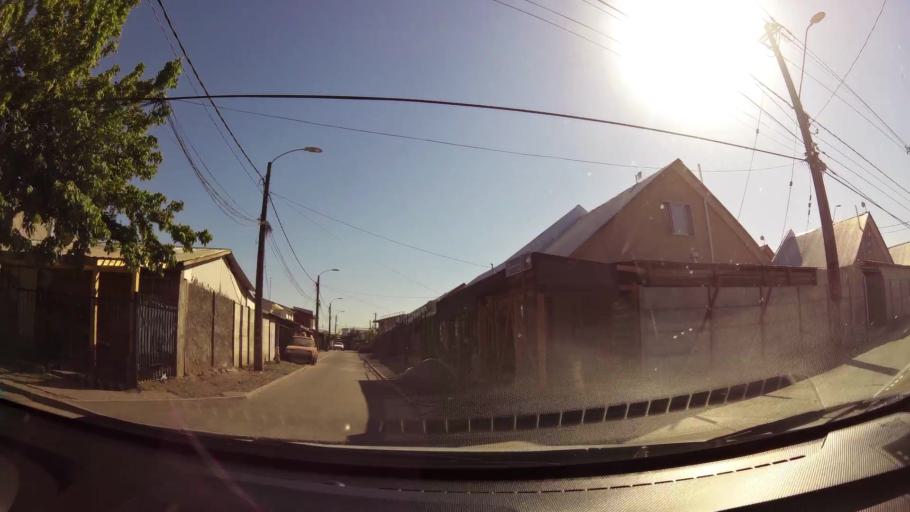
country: CL
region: Maule
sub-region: Provincia de Curico
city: Curico
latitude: -34.9965
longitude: -71.2591
